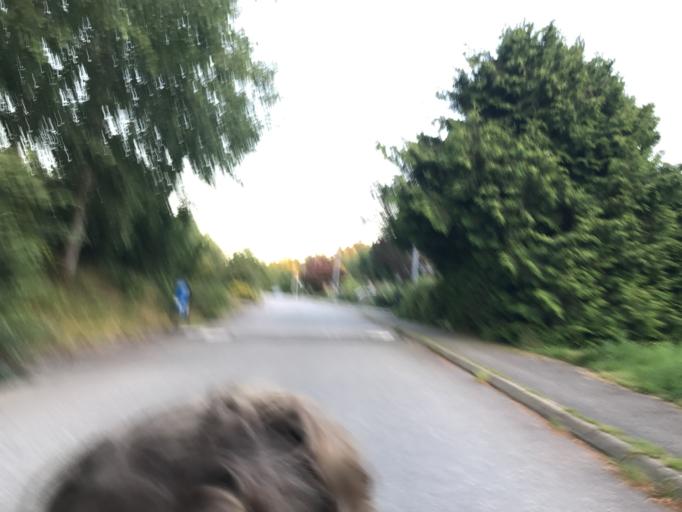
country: SE
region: Vaestra Goetaland
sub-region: Lerums Kommun
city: Lerum
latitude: 57.7799
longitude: 12.2500
